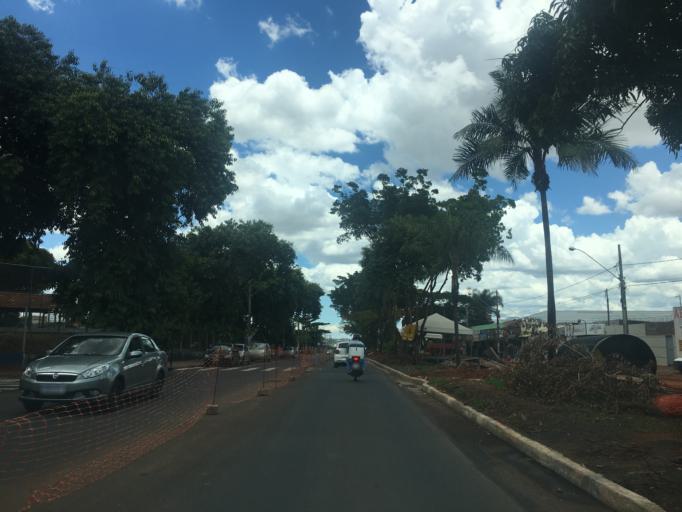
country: BR
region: Minas Gerais
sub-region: Uberlandia
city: Uberlandia
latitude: -18.9425
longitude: -48.3096
